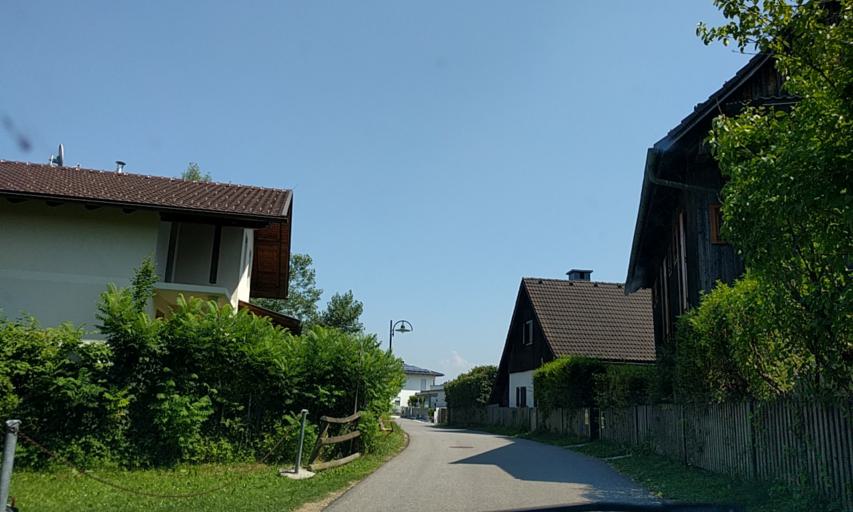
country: AT
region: Carinthia
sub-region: Politischer Bezirk Villach Land
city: Finkenstein am Faaker See
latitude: 46.5693
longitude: 13.9082
